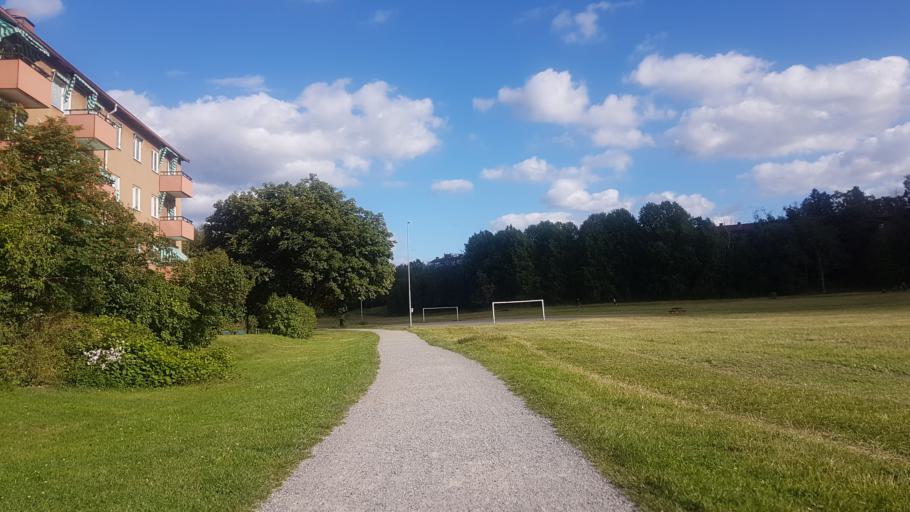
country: SE
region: Stockholm
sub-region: Stockholms Kommun
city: OEstermalm
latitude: 59.2895
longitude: 18.1107
